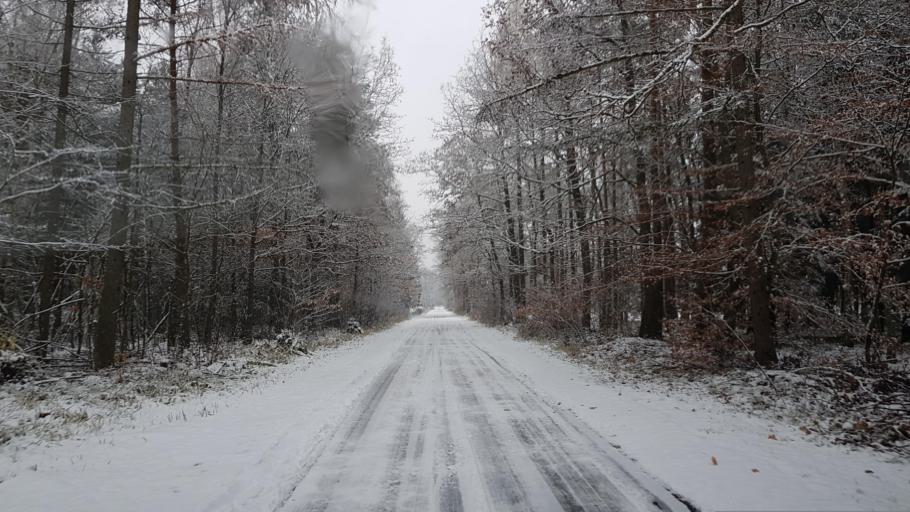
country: PL
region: West Pomeranian Voivodeship
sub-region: Powiat lobeski
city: Resko
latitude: 53.7857
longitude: 15.5321
